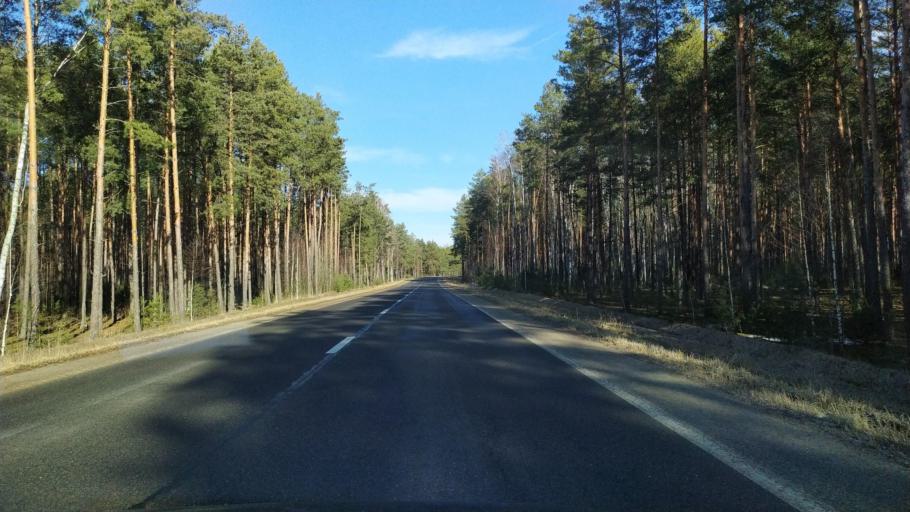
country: BY
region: Brest
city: Zhabinka
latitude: 52.4515
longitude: 24.1371
